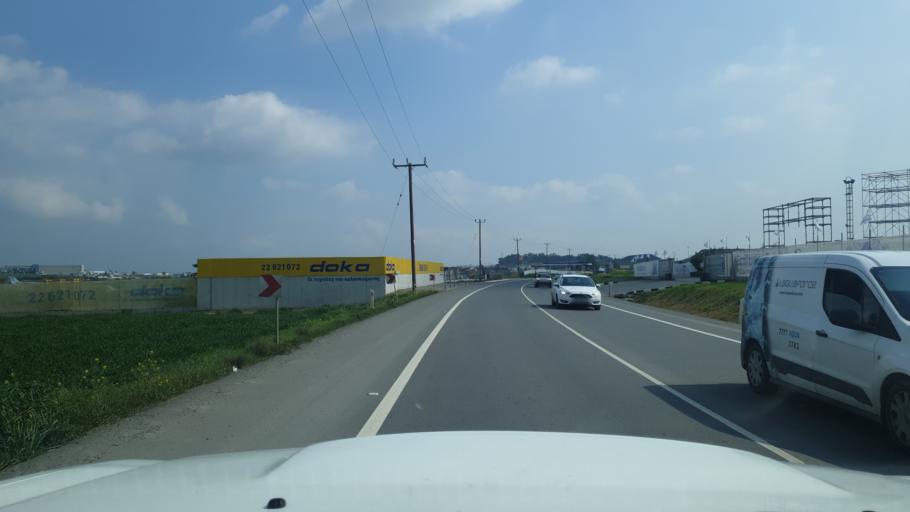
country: CY
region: Lefkosia
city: Tseri
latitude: 35.0580
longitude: 33.3709
